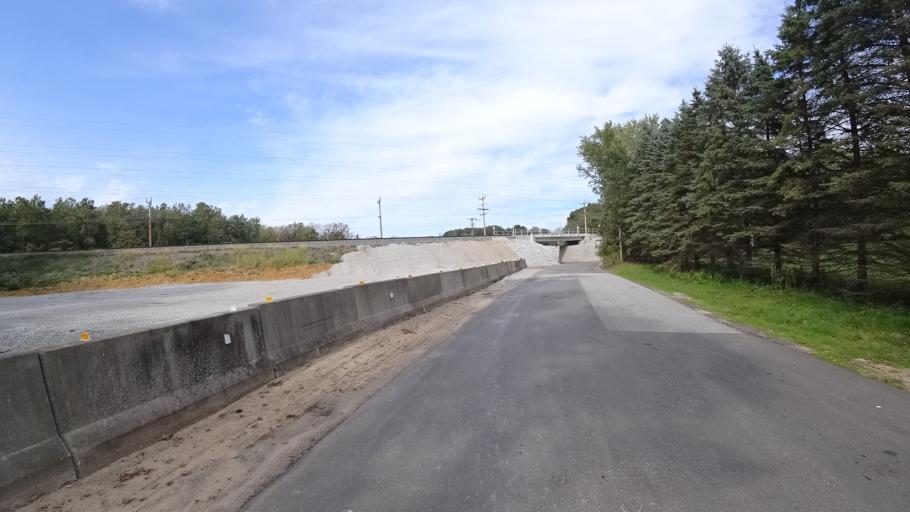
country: US
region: Indiana
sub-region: LaPorte County
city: Trail Creek
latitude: 41.7095
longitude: -86.8553
